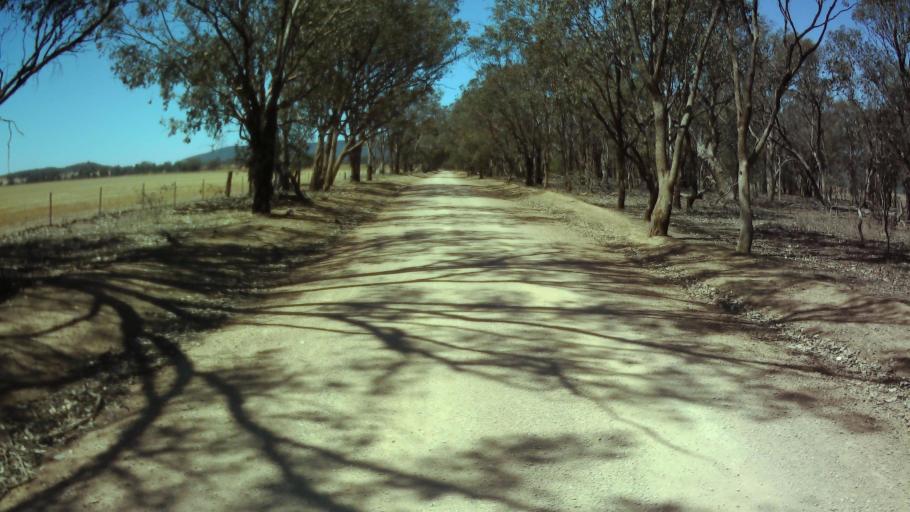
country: AU
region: New South Wales
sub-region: Weddin
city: Grenfell
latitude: -33.9193
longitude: 148.0789
